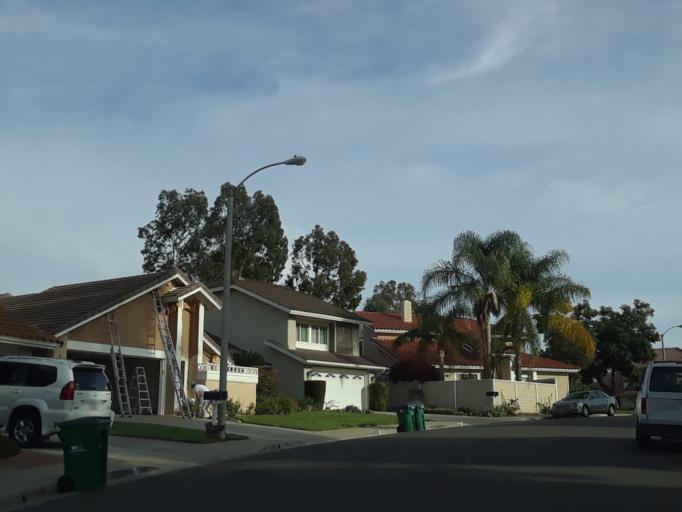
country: US
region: California
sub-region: Orange County
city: North Tustin
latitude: 33.7181
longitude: -117.7533
